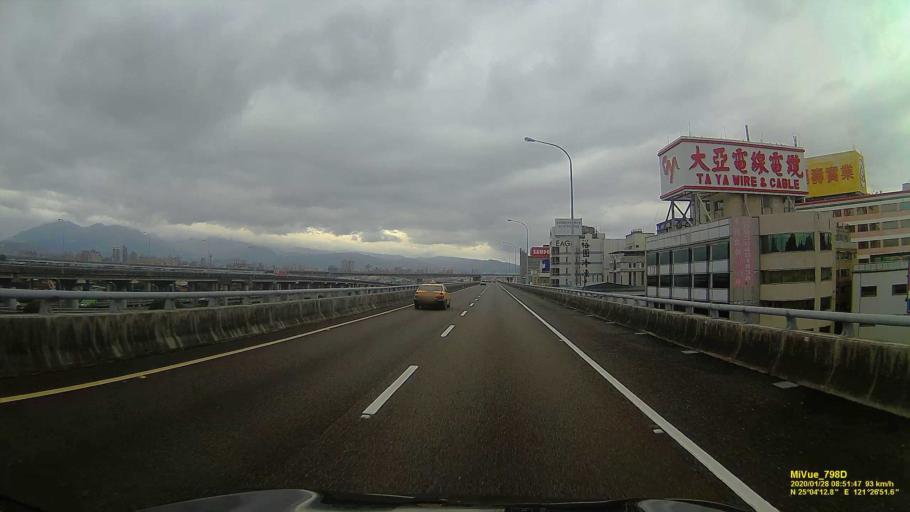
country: TW
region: Taipei
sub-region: Taipei
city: Banqiao
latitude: 25.0704
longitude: 121.4484
